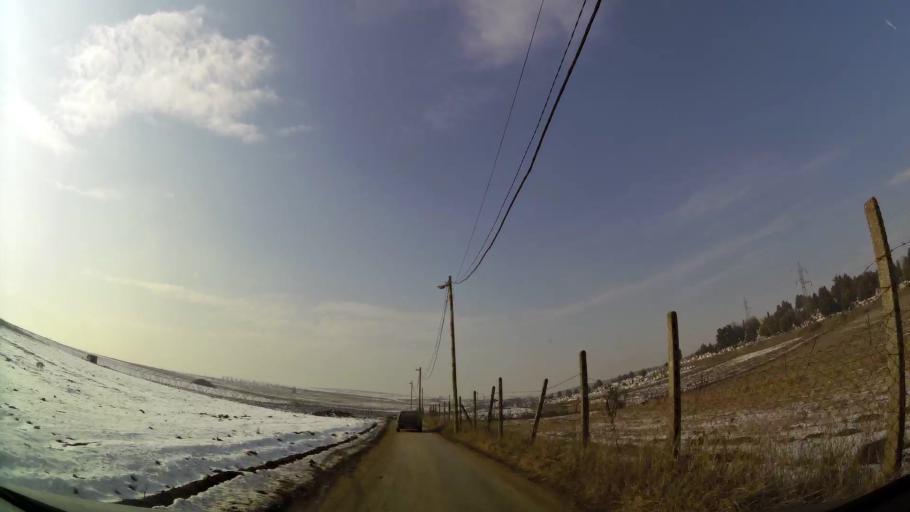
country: MK
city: Creshevo
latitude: 42.0137
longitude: 21.4940
